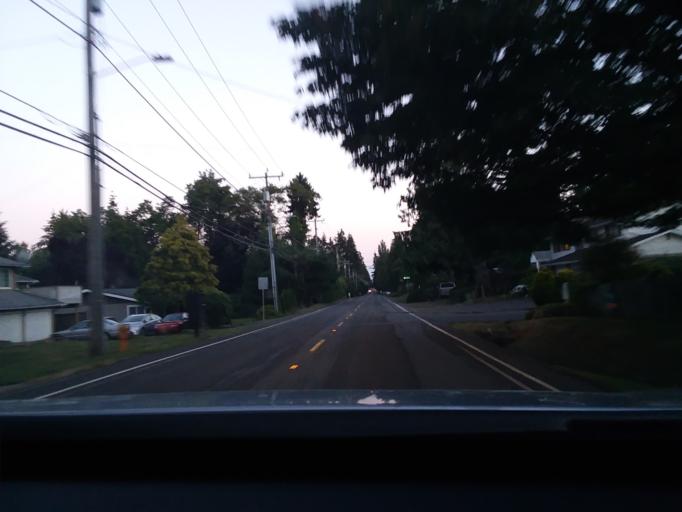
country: US
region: Washington
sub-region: King County
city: Shoreline
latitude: 47.7605
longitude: -122.3404
